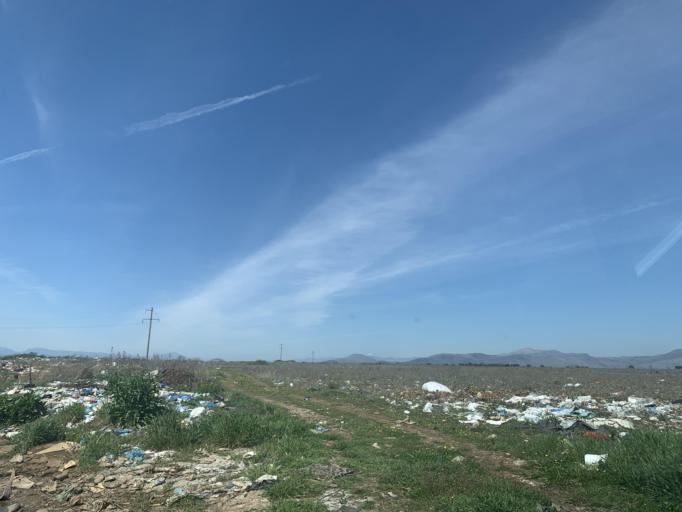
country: AL
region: Shkoder
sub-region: Rrethi i Malesia e Madhe
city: Koplik
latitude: 42.2289
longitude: 19.4365
